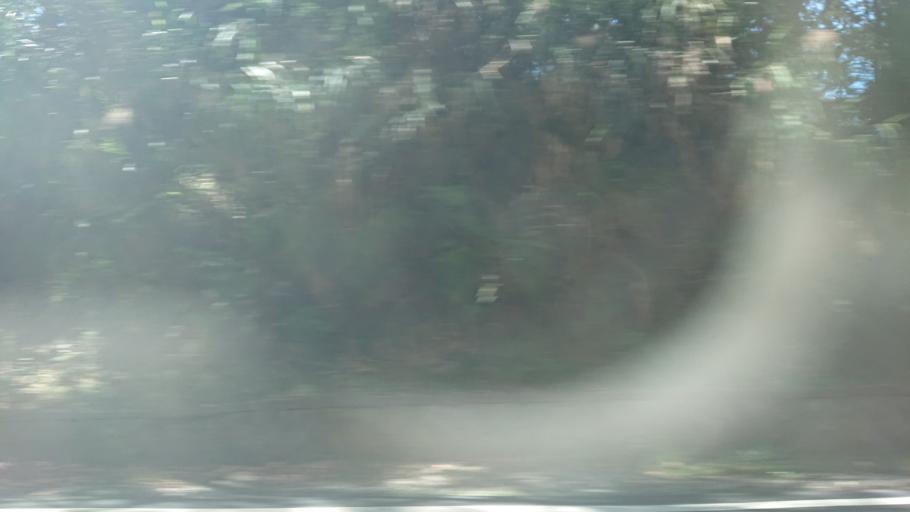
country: TW
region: Taiwan
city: Lugu
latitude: 23.4908
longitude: 120.8191
